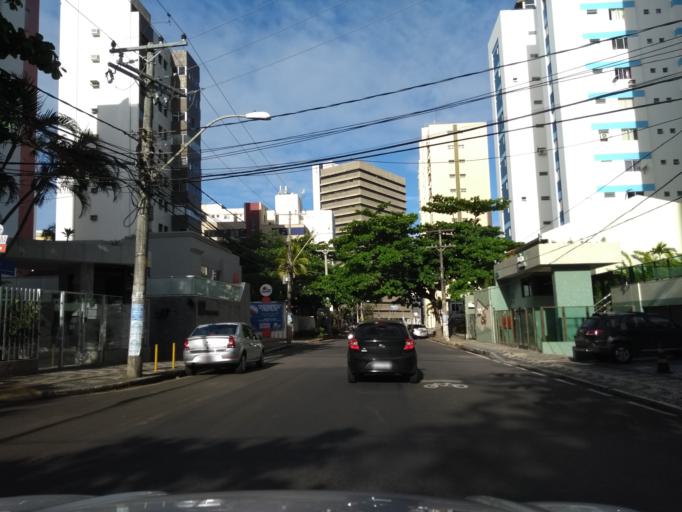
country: BR
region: Bahia
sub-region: Salvador
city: Salvador
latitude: -13.0020
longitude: -38.4564
